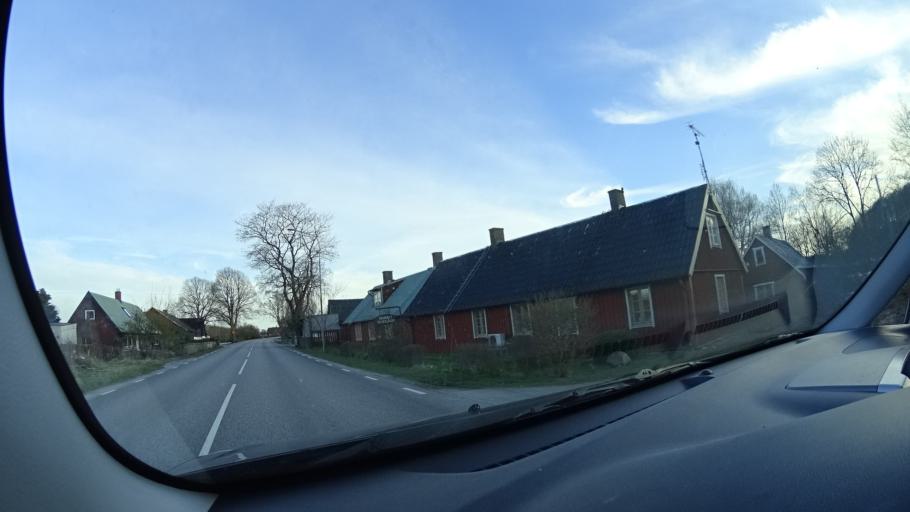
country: SE
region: Skane
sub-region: Eslovs Kommun
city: Stehag
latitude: 55.9735
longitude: 13.3290
